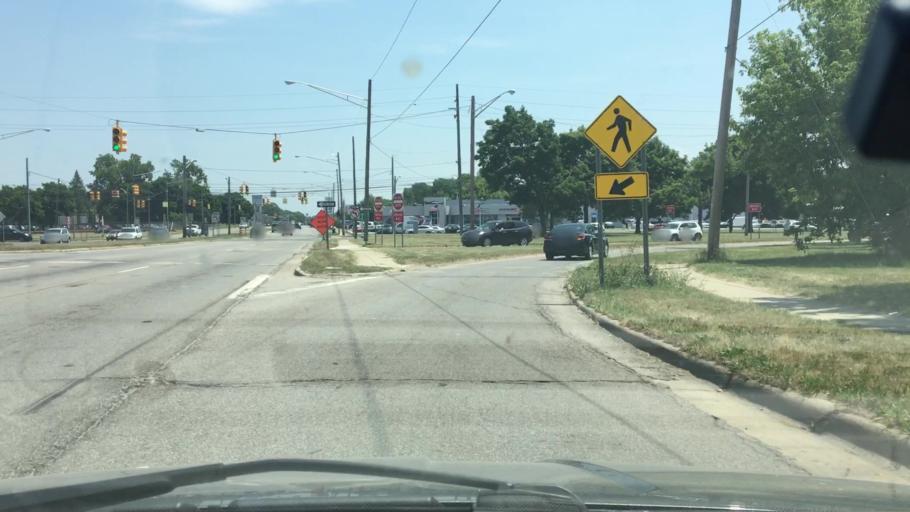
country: US
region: Michigan
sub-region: Wayne County
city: Redford
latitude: 42.3711
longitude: -83.2772
